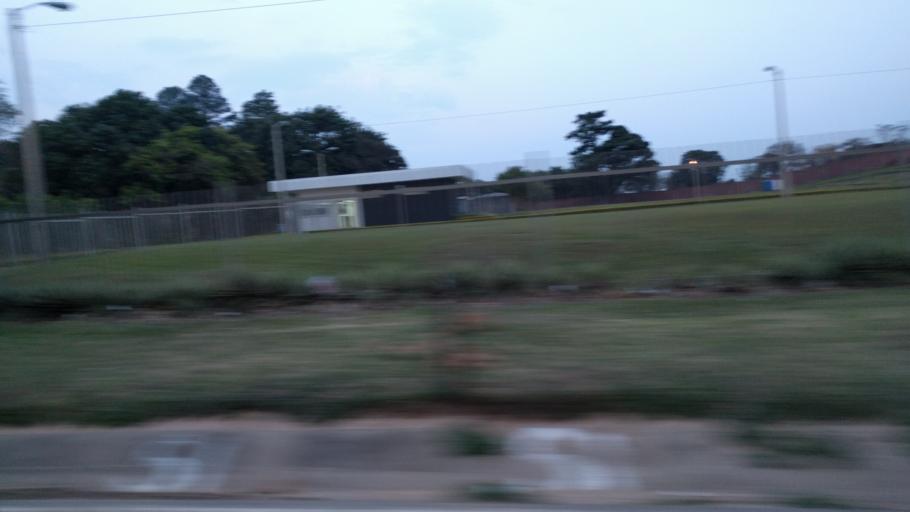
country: BO
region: Santa Cruz
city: Santa Rita
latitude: -17.8859
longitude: -63.2967
